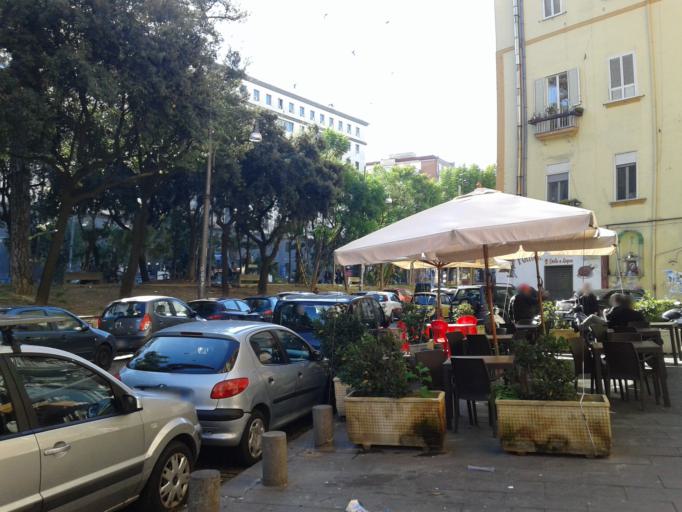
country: IT
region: Campania
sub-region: Provincia di Napoli
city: Napoli
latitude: 40.8550
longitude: 14.2541
